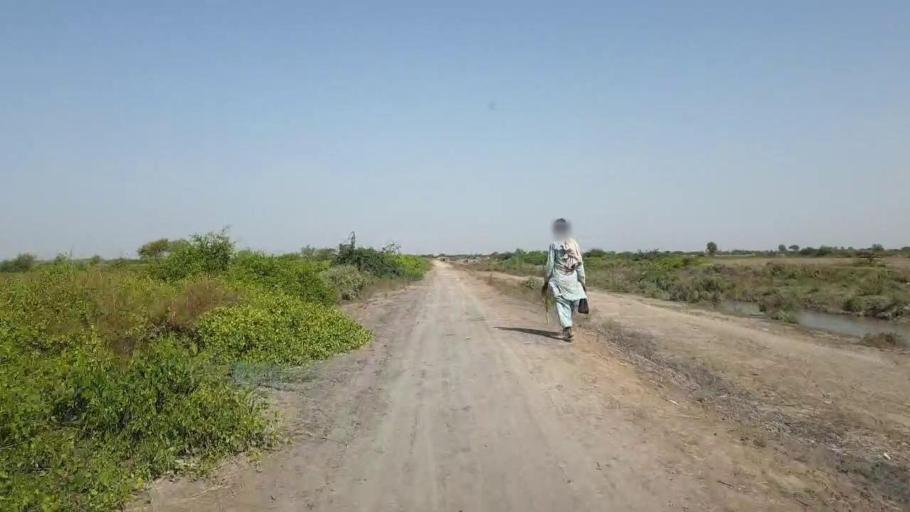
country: PK
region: Sindh
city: Tando Bago
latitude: 24.7050
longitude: 69.0711
